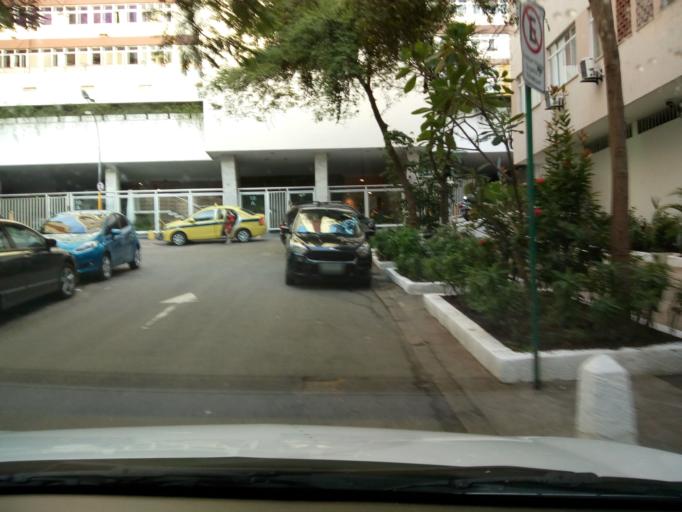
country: BR
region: Rio de Janeiro
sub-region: Rio De Janeiro
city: Rio de Janeiro
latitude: -22.9811
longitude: -43.1995
